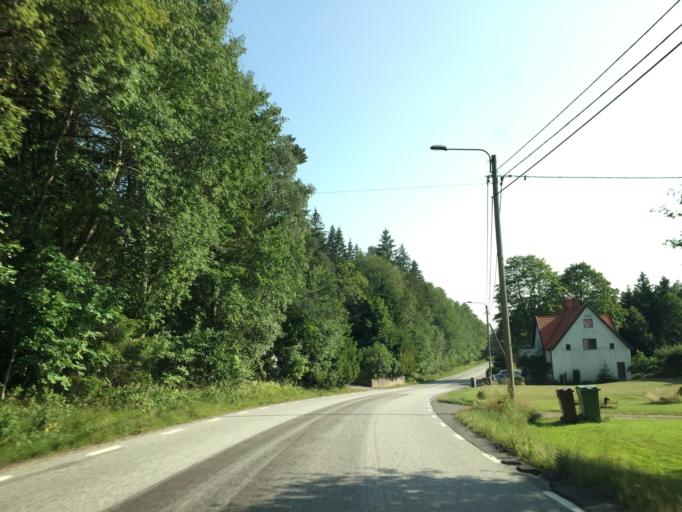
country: SE
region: Vaestra Goetaland
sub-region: Trollhattan
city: Trollhattan
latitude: 58.2979
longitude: 12.2521
